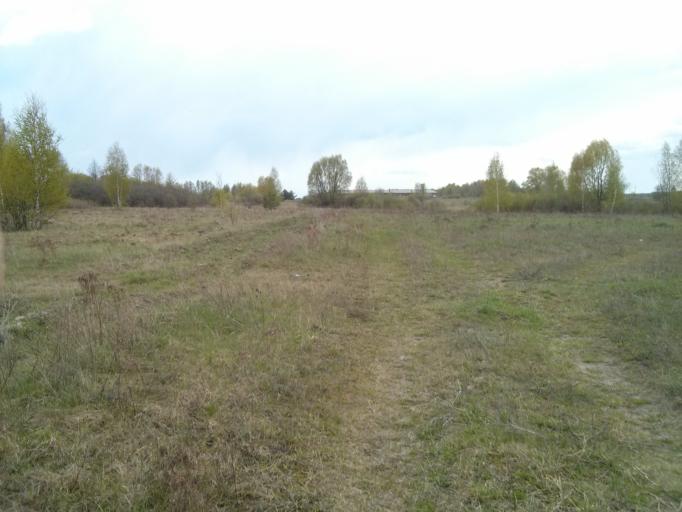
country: RU
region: Nizjnij Novgorod
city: Shimorskoye
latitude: 55.3082
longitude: 41.8446
